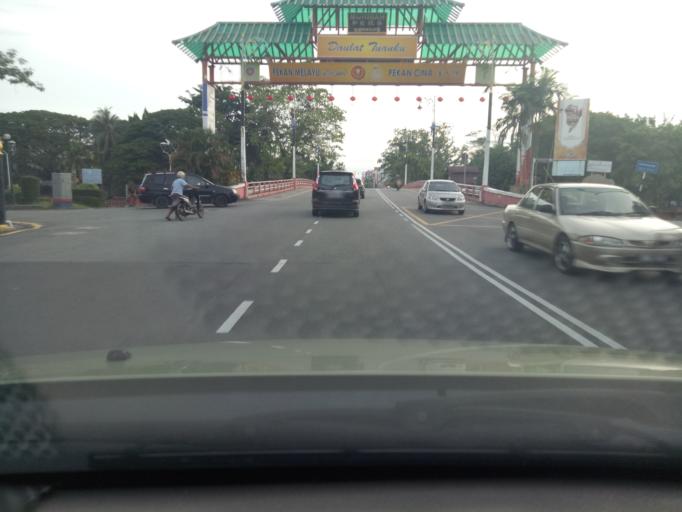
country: MY
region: Kedah
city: Alor Setar
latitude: 6.1161
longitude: 100.3638
